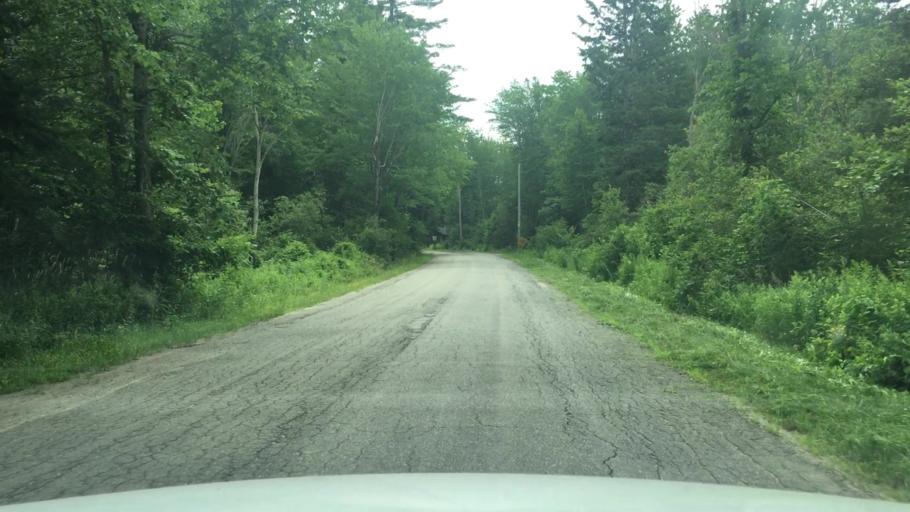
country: US
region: Maine
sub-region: Kennebec County
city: Albion
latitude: 44.4599
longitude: -69.3338
